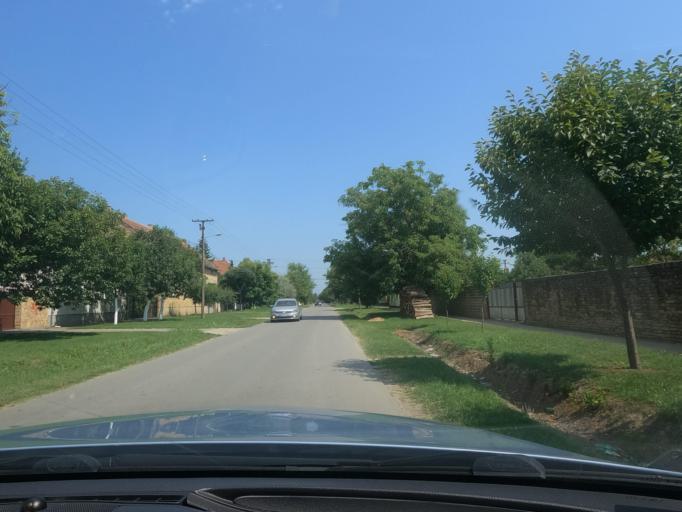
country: RS
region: Autonomna Pokrajina Vojvodina
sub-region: Juznobacki Okrug
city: Kovilj
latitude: 45.2223
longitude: 20.0289
